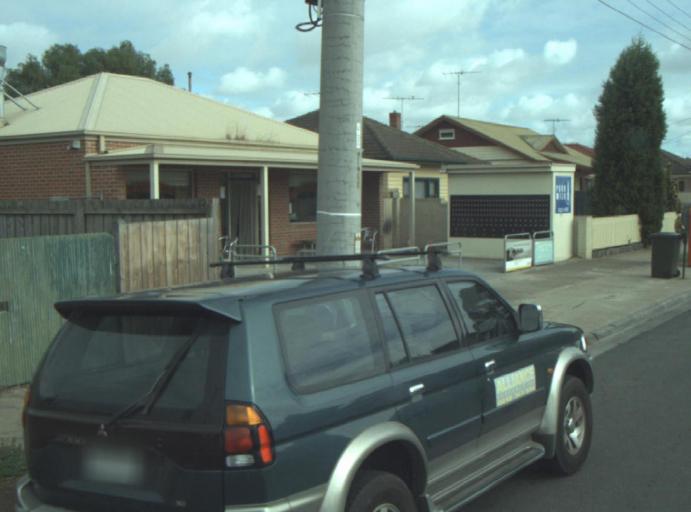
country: AU
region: Victoria
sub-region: Greater Geelong
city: Bell Park
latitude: -38.1001
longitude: 144.3717
